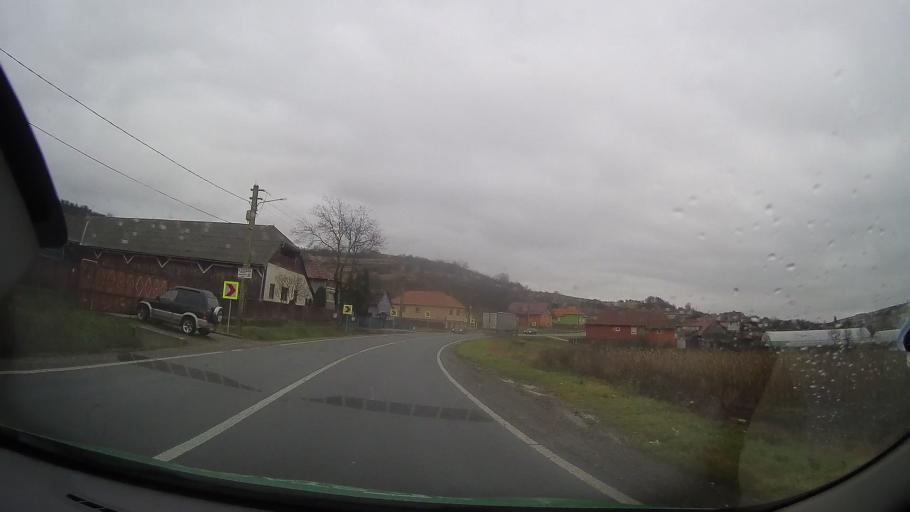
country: RO
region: Mures
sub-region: Comuna Lunca
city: Lunca
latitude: 46.8565
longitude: 24.5672
